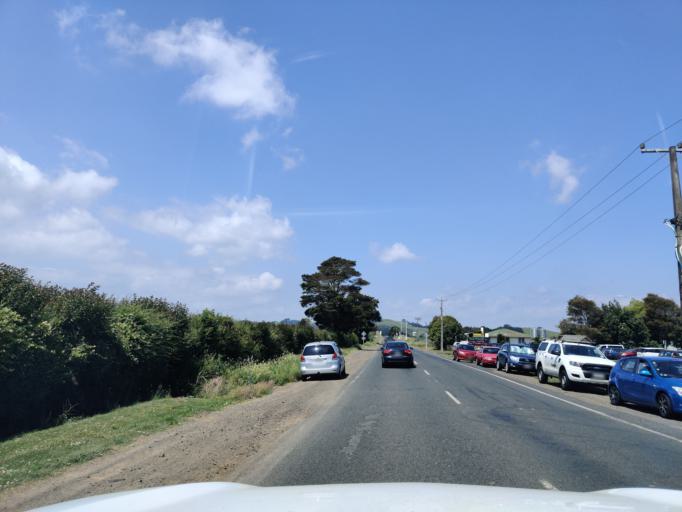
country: NZ
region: Auckland
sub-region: Auckland
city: Pukekohe East
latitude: -37.2395
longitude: 174.9517
